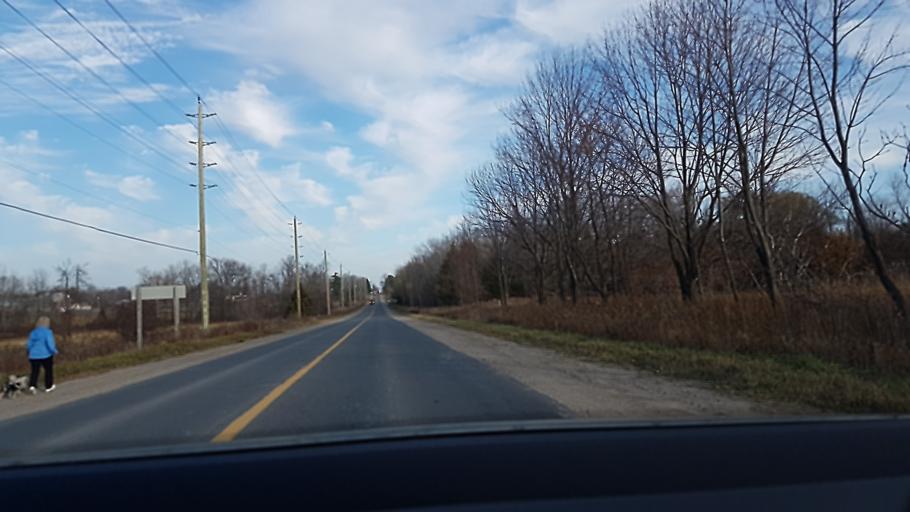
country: CA
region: Ontario
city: Barrie
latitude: 44.3725
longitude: -79.5786
